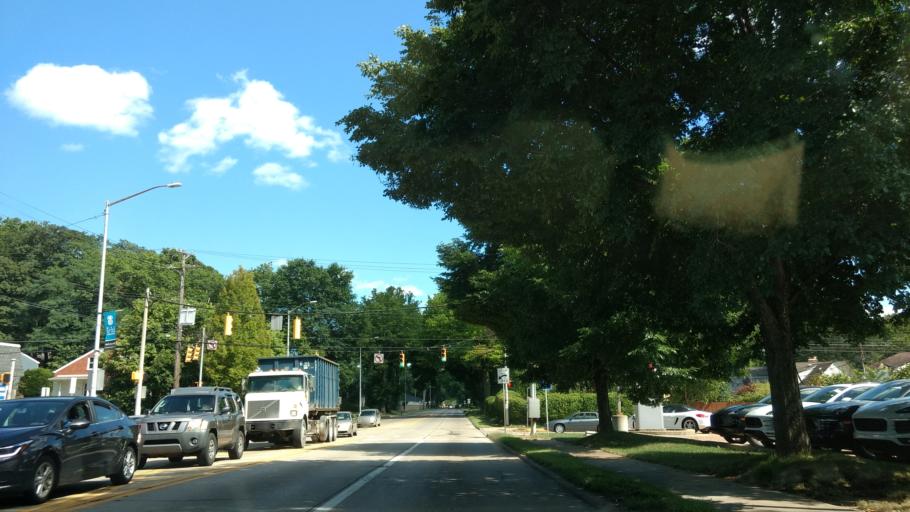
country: US
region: Pennsylvania
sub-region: Allegheny County
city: Sewickley
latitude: 40.5361
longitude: -80.1836
